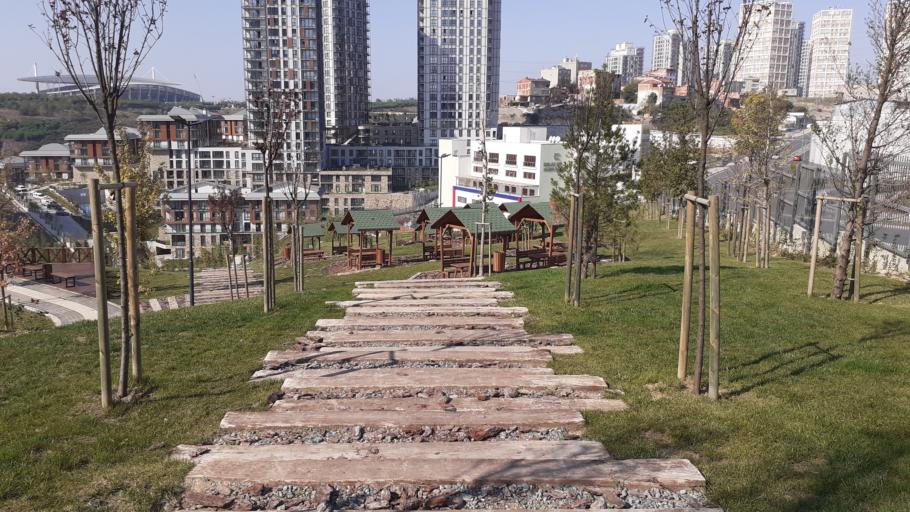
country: TR
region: Istanbul
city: Basaksehir
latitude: 41.0677
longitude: 28.7797
